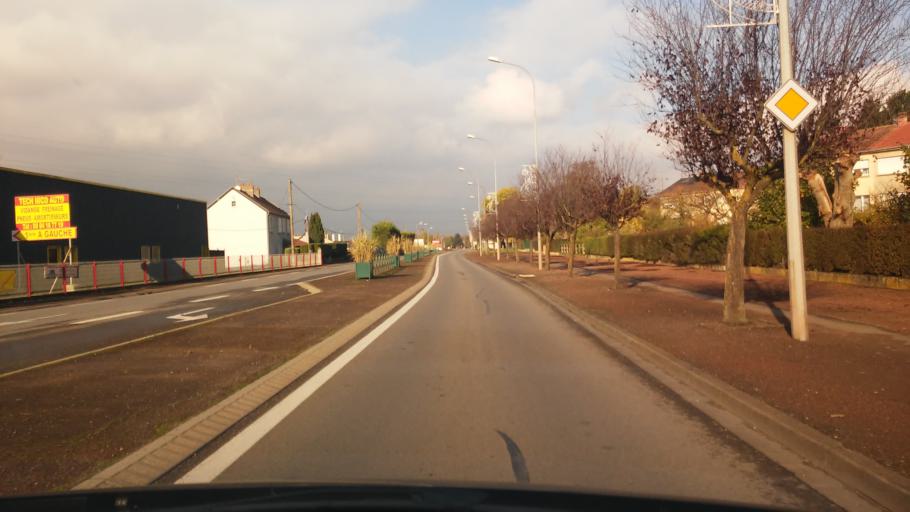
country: FR
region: Lorraine
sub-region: Departement de la Moselle
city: Mondelange
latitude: 49.2718
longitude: 6.1705
